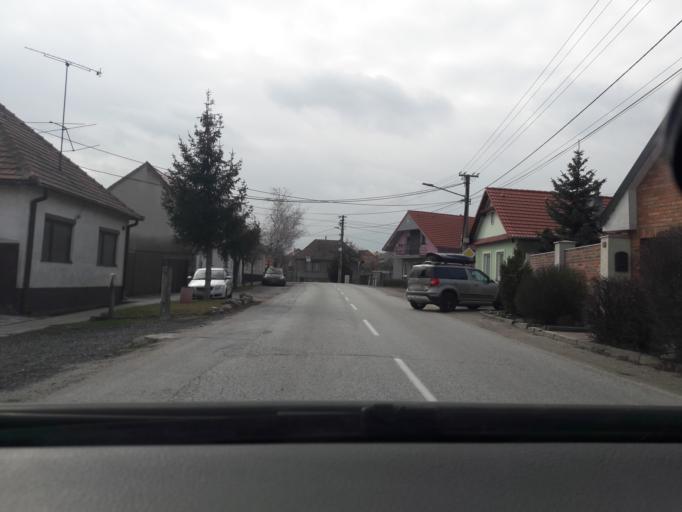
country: SK
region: Trnavsky
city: Smolenice
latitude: 48.4383
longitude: 17.4271
